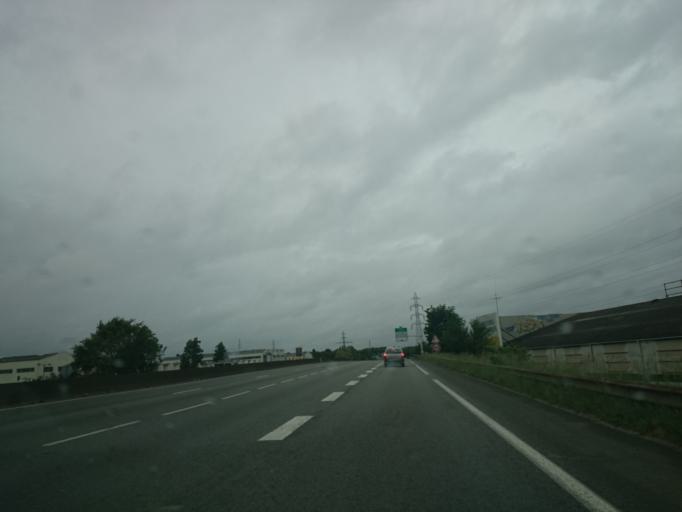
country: FR
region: Brittany
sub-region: Departement d'Ille-et-Vilaine
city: Vezin-le-Coquet
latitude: 48.1062
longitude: -1.7169
